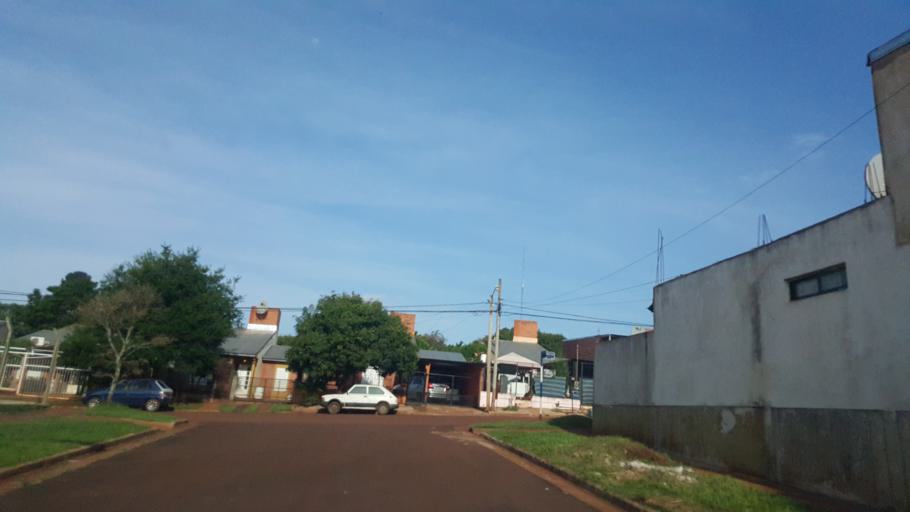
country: AR
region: Misiones
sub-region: Departamento de Capital
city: Posadas
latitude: -27.4249
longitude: -55.9232
